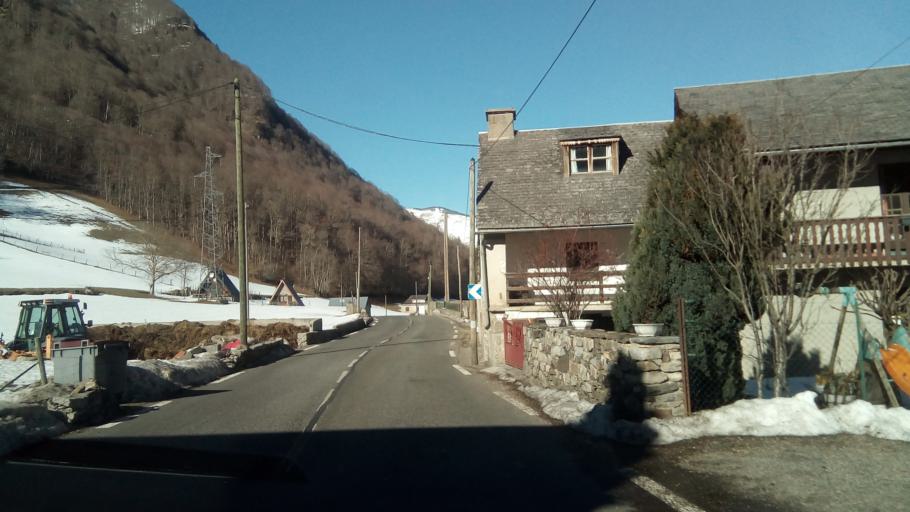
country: FR
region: Midi-Pyrenees
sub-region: Departement des Hautes-Pyrenees
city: Campan
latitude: 42.9542
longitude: 0.2292
